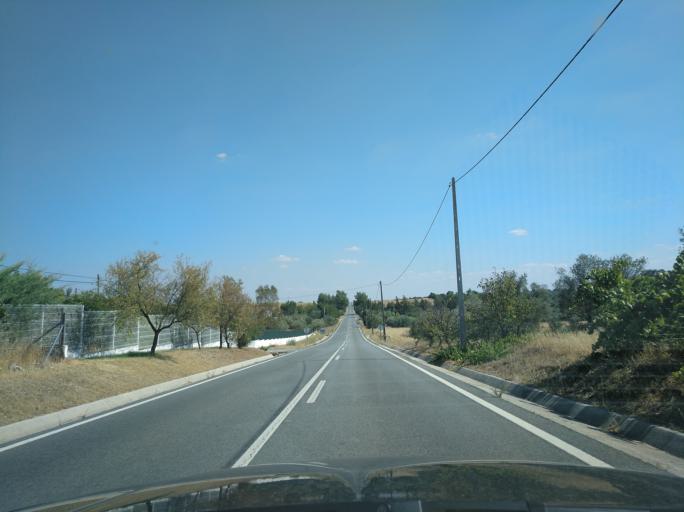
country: PT
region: Portalegre
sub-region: Campo Maior
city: Campo Maior
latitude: 38.9645
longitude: -7.0481
